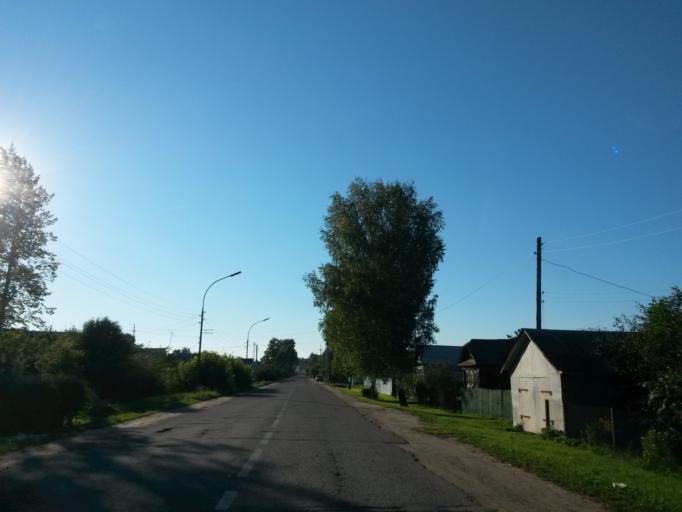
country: RU
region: Jaroslavl
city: Gavrilov-Yam
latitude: 57.2962
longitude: 39.8740
